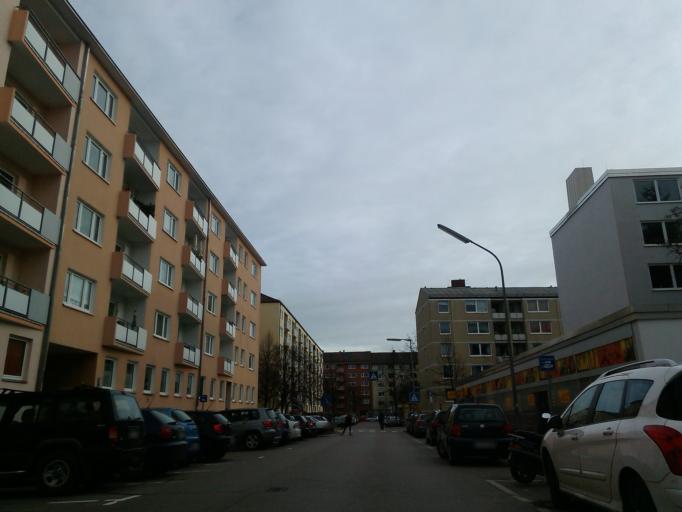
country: DE
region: Bavaria
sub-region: Upper Bavaria
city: Munich
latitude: 48.1184
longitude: 11.5460
